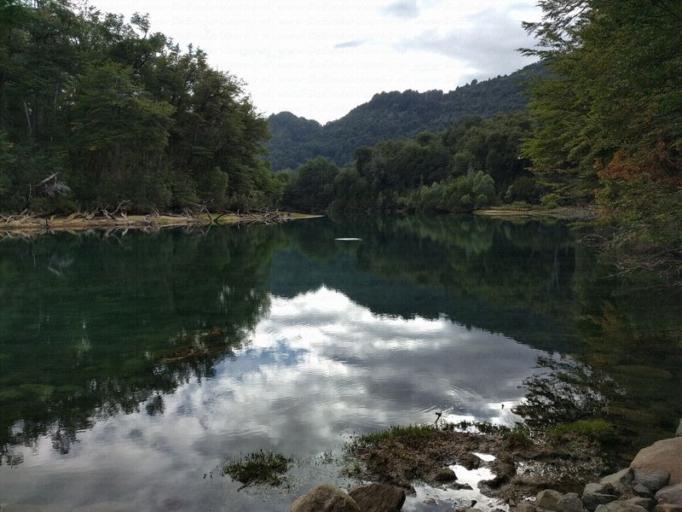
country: AR
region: Chubut
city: Trevelin
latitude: -42.7456
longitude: -71.7456
